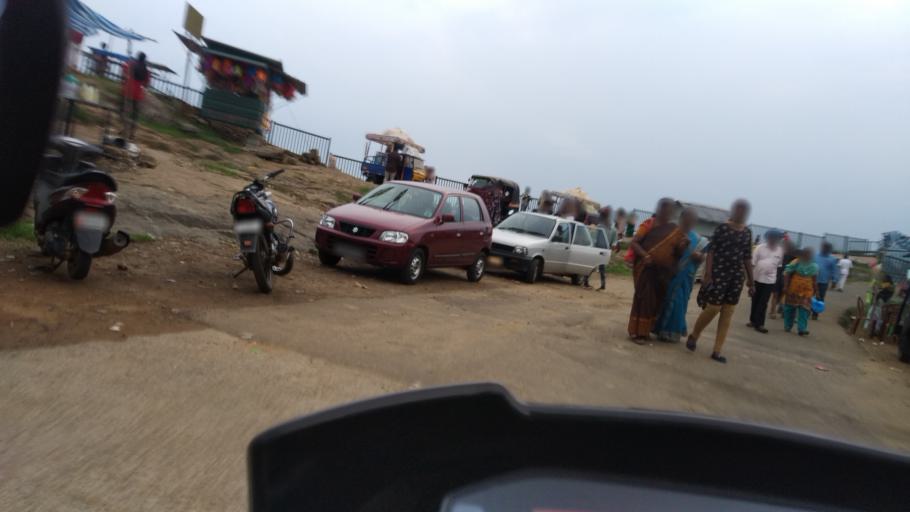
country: IN
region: Tamil Nadu
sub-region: Theni
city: Gudalur
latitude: 9.5504
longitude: 77.0310
